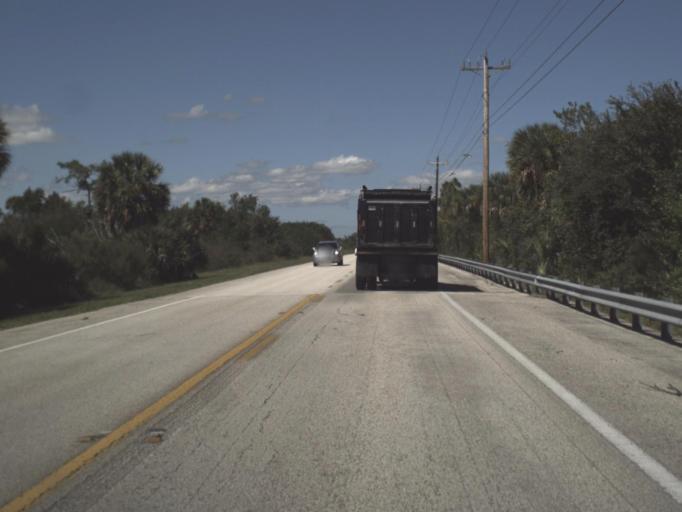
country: US
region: Florida
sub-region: Collier County
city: Marco
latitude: 25.9625
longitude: -81.5206
